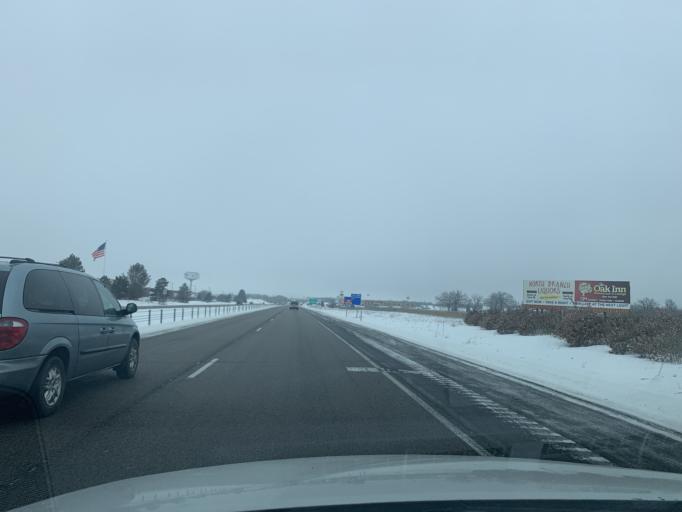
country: US
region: Minnesota
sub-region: Chisago County
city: North Branch
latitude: 45.5023
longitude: -92.9933
